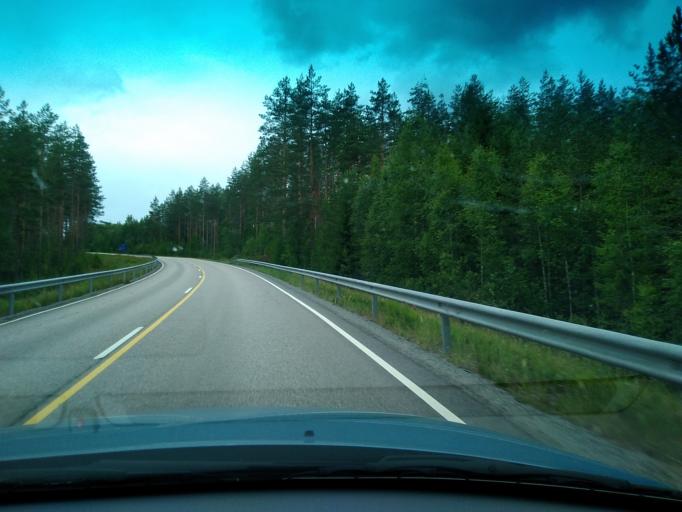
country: FI
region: Central Finland
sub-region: Saarijaervi-Viitasaari
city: Pylkoenmaeki
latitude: 62.5931
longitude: 24.6014
